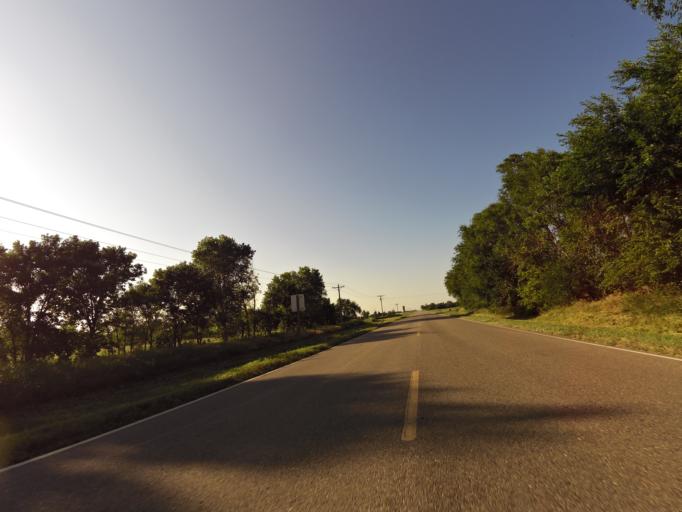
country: US
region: Kansas
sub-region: Reno County
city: Buhler
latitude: 38.1724
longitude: -97.8486
